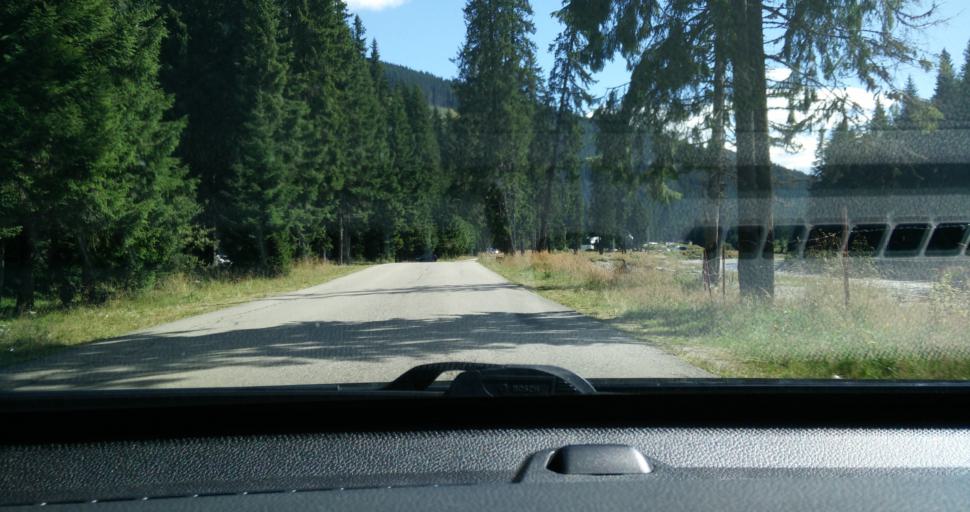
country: RO
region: Hunedoara
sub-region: Oras Petrila
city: Petrila
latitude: 45.4335
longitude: 23.6256
